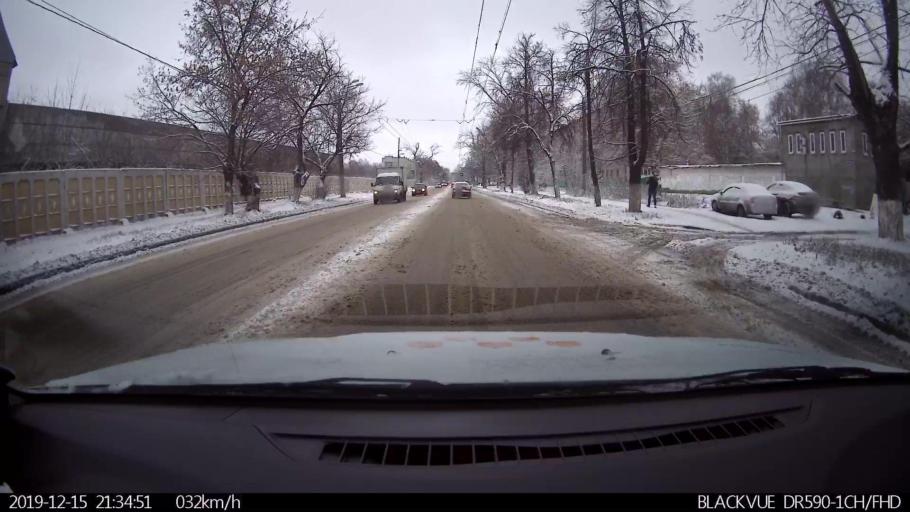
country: RU
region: Nizjnij Novgorod
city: Burevestnik
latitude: 56.2373
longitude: 43.8724
